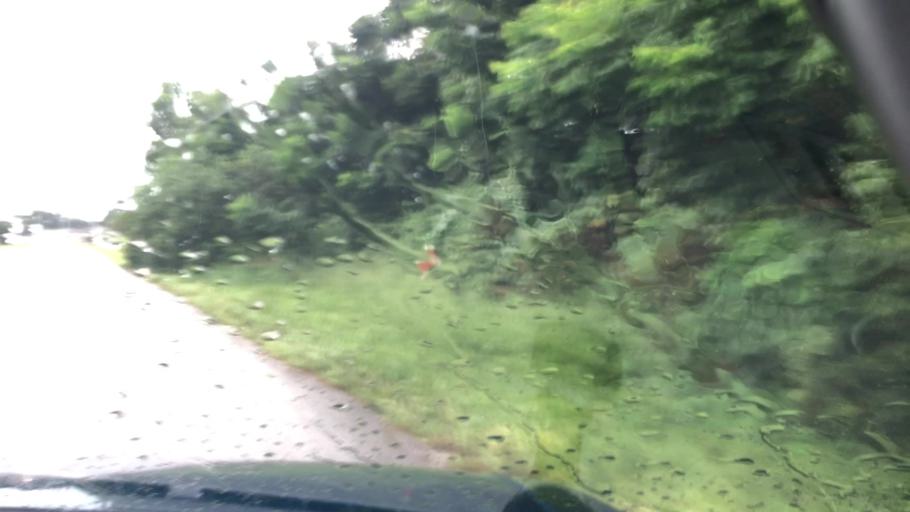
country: US
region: Florida
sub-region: Lake County
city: Eustis
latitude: 28.8791
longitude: -81.7371
